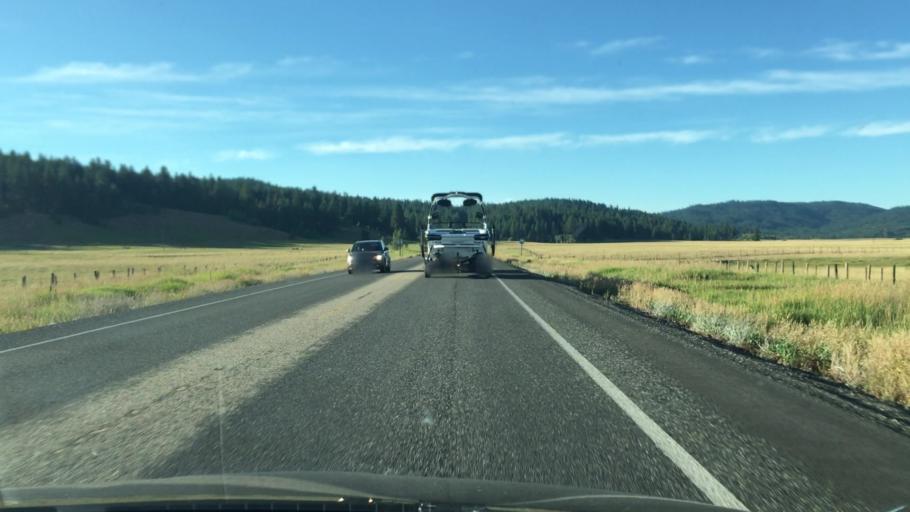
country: US
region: Idaho
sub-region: Valley County
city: Cascade
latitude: 44.5490
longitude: -116.0270
